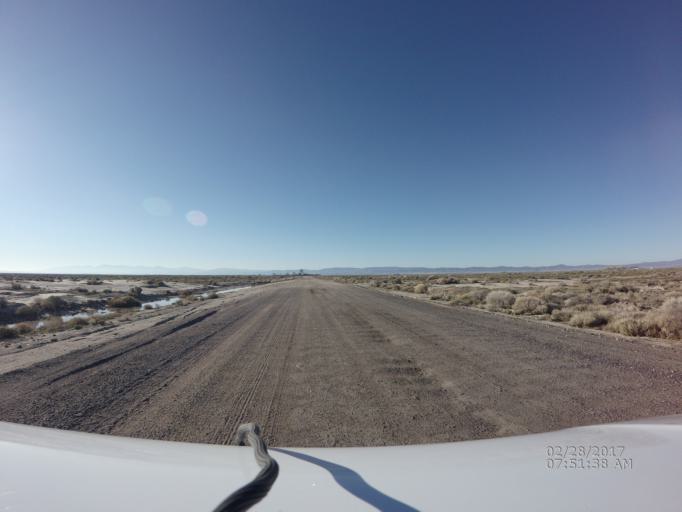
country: US
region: California
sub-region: Kern County
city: Rosamond
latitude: 34.8129
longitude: -118.1848
